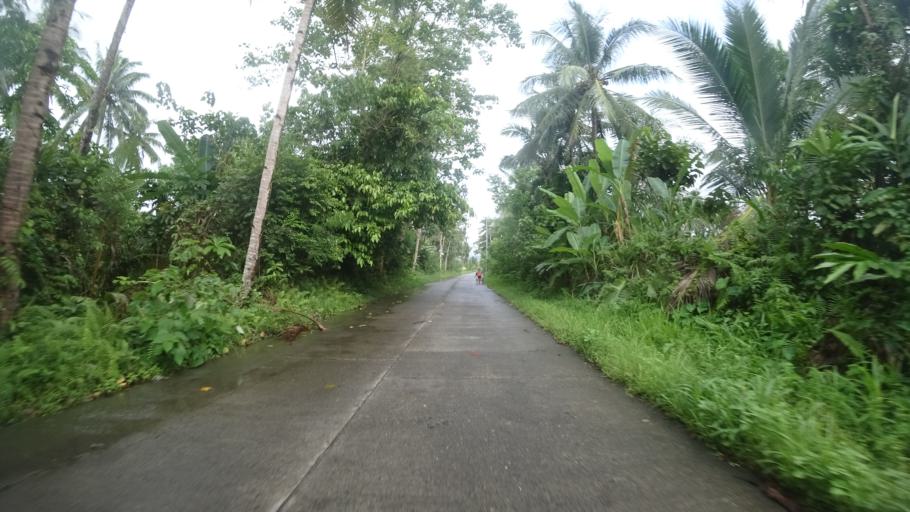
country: PH
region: Eastern Visayas
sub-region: Province of Leyte
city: Bugho
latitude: 10.8207
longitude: 124.9417
